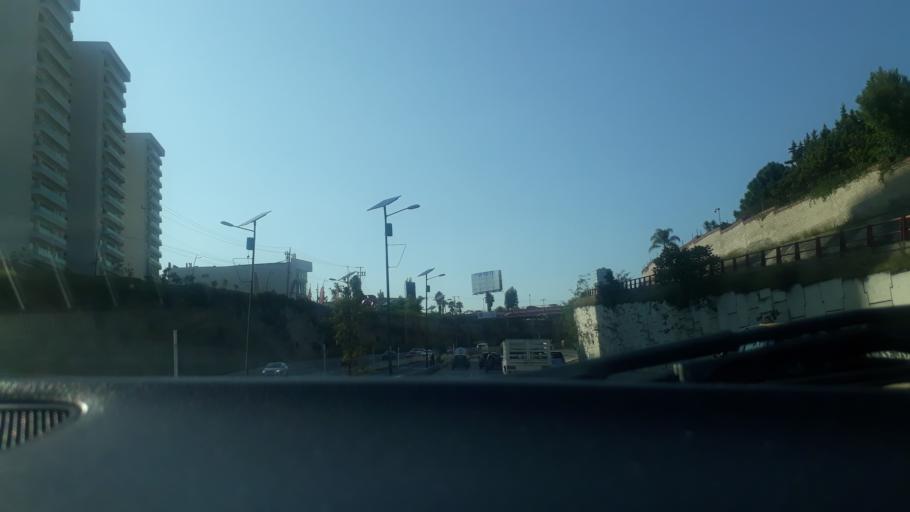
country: MX
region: Puebla
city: Tlazcalancingo
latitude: 18.9988
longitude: -98.2590
